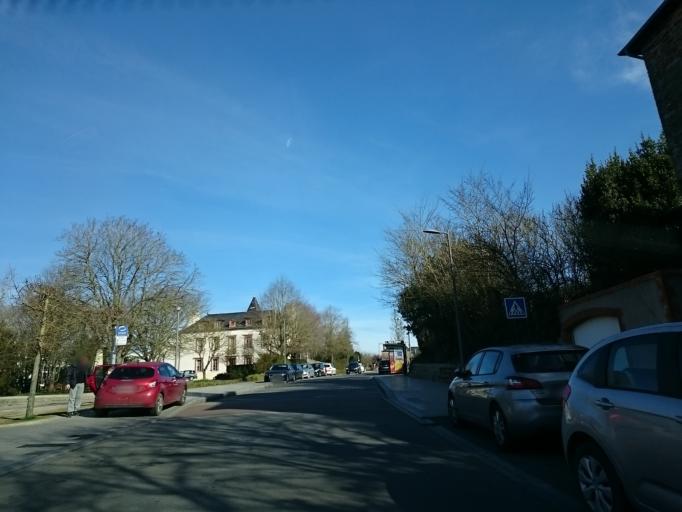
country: FR
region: Brittany
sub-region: Departement d'Ille-et-Vilaine
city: Vern-sur-Seiche
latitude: 48.0469
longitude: -1.6026
